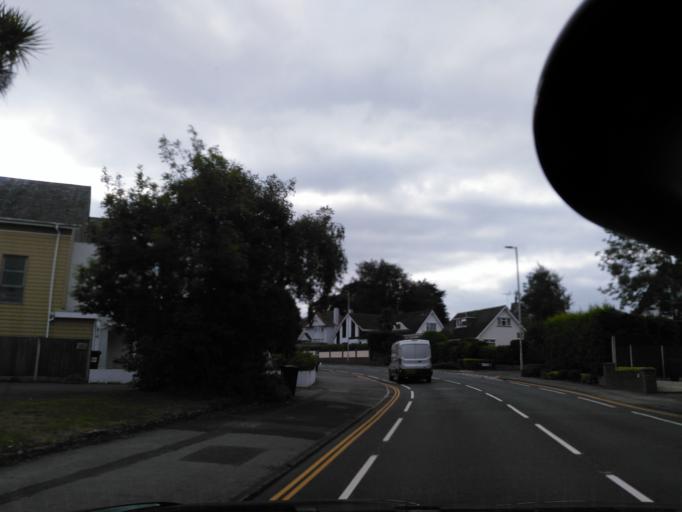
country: GB
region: England
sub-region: Dorset
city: Parkstone
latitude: 50.7141
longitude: -1.9530
